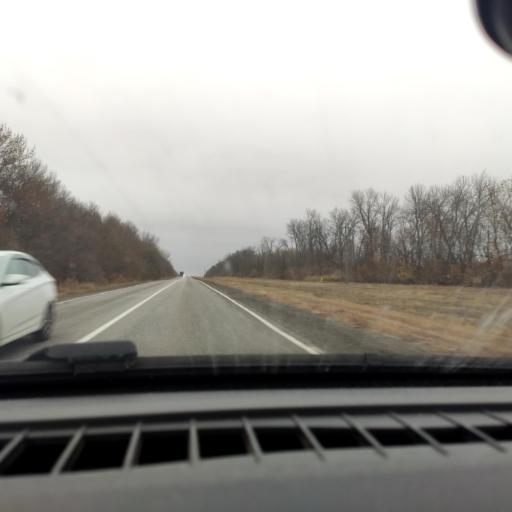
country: RU
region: Voronezj
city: Uryv-Pokrovka
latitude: 51.1060
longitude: 39.0209
